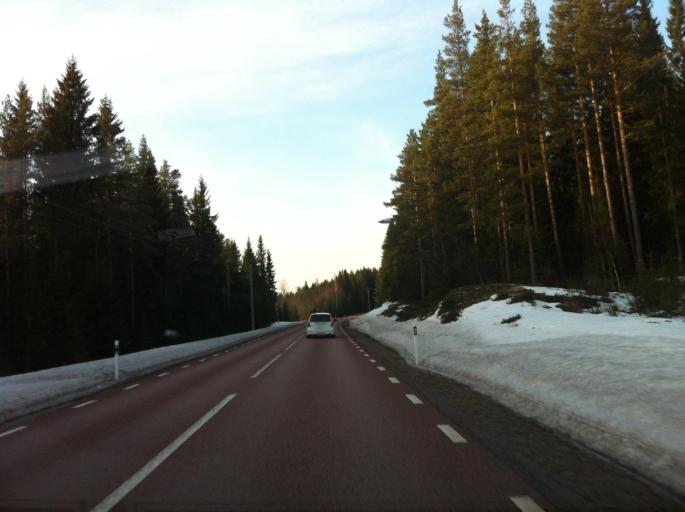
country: SE
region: Vaermland
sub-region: Filipstads Kommun
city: Lesjofors
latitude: 60.2218
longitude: 14.1858
